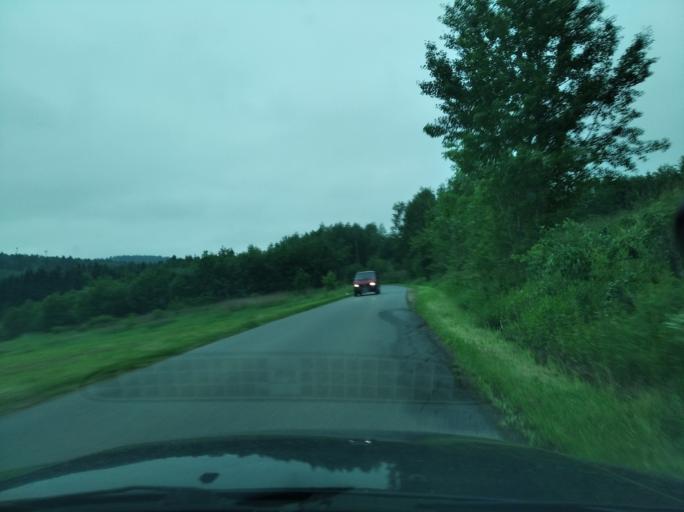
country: PL
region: Subcarpathian Voivodeship
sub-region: Powiat brzozowski
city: Orzechowka
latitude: 49.7267
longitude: 21.9274
